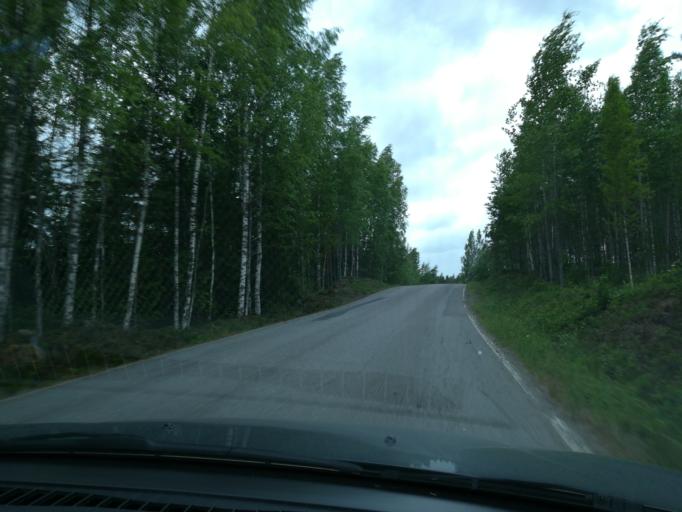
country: FI
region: South Karelia
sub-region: Lappeenranta
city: Savitaipale
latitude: 61.3209
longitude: 27.4889
